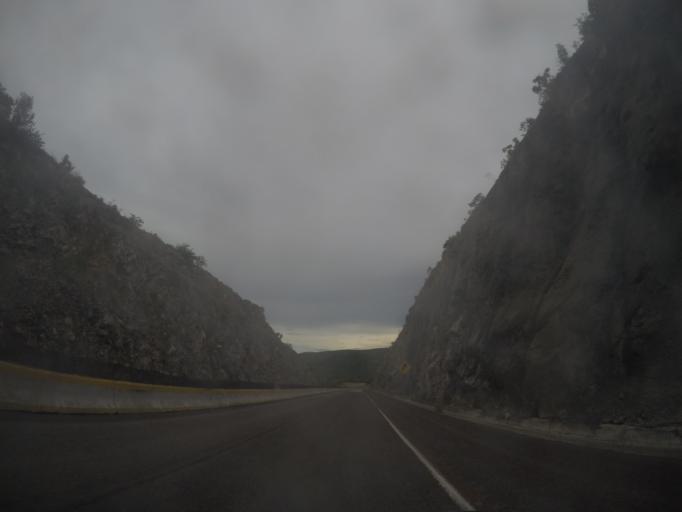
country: MX
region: Guerrero
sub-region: Eduardo Neri
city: Tlanipatla
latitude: 17.8560
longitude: -99.4226
